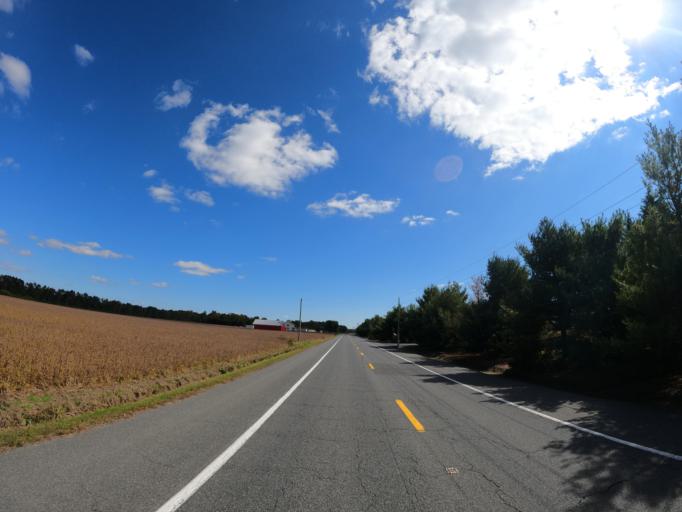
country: US
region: Delaware
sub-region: Sussex County
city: Bridgeville
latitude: 38.8244
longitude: -75.6373
